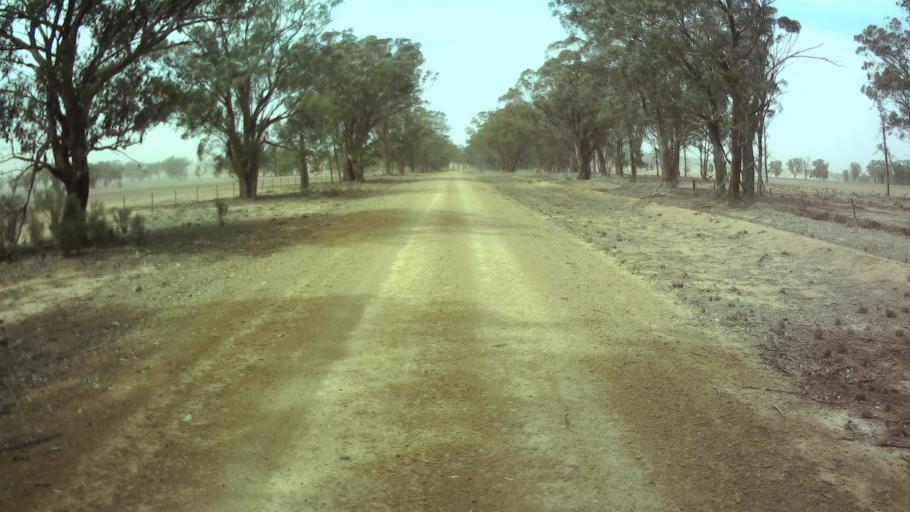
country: AU
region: New South Wales
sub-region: Weddin
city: Grenfell
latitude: -33.7375
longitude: 147.9615
